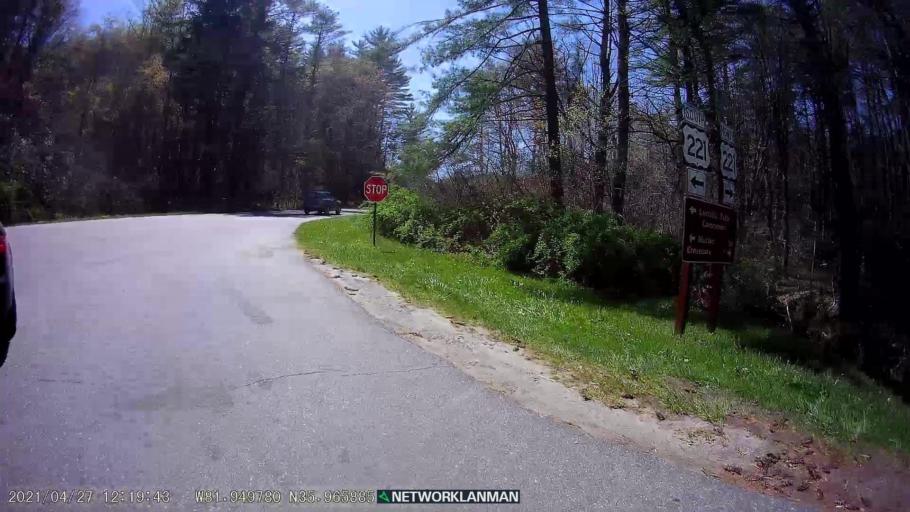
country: US
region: North Carolina
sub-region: Avery County
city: Newland
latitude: 35.9659
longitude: -81.9501
